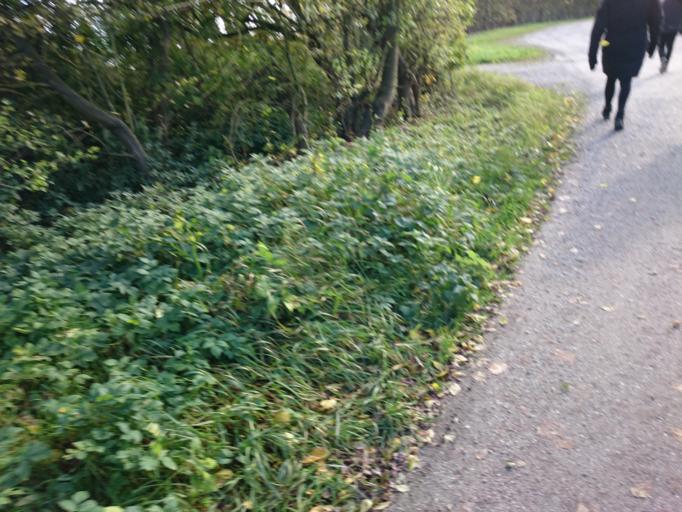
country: DK
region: South Denmark
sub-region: Odense Kommune
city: Hojby
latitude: 55.3295
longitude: 10.4314
